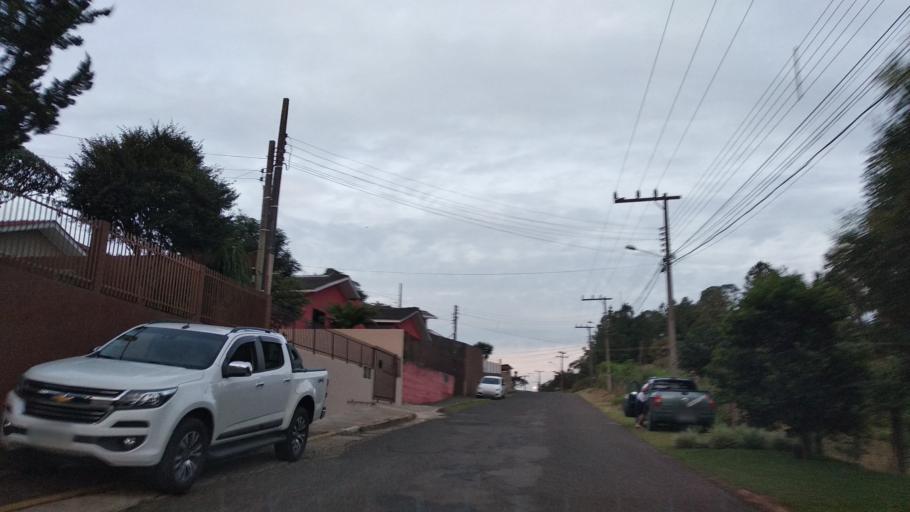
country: BR
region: Santa Catarina
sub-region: Videira
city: Videira
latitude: -26.9951
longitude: -51.1821
